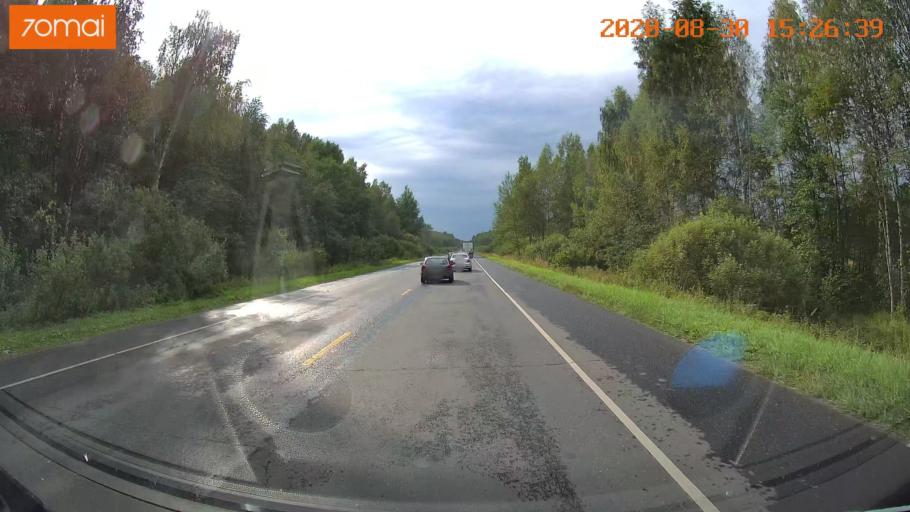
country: RU
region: Ivanovo
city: Rodniki
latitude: 57.0870
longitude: 41.6291
